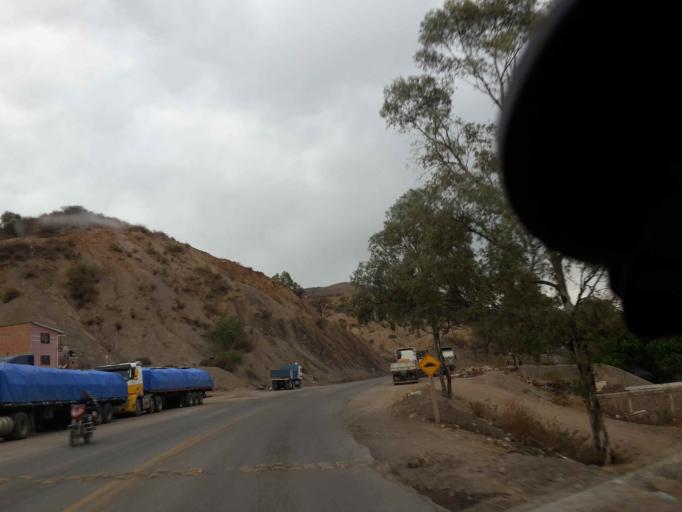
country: BO
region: Cochabamba
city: Sipe Sipe
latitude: -17.5554
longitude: -66.3428
